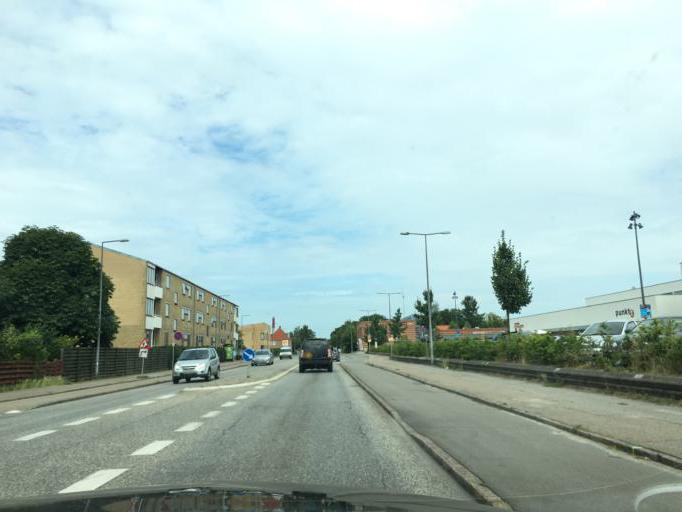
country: DK
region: Capital Region
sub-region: Horsholm Kommune
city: Horsholm
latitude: 55.8877
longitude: 12.4971
